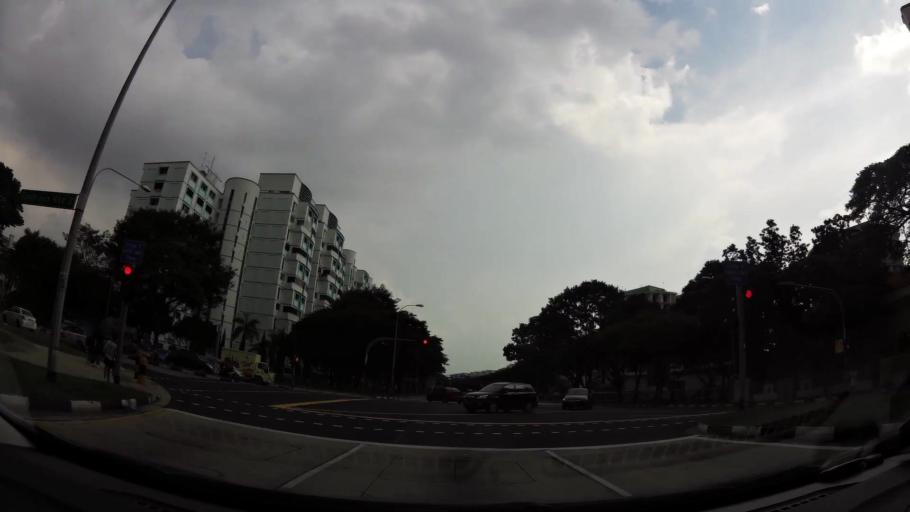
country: SG
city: Singapore
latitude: 1.3491
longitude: 103.9284
